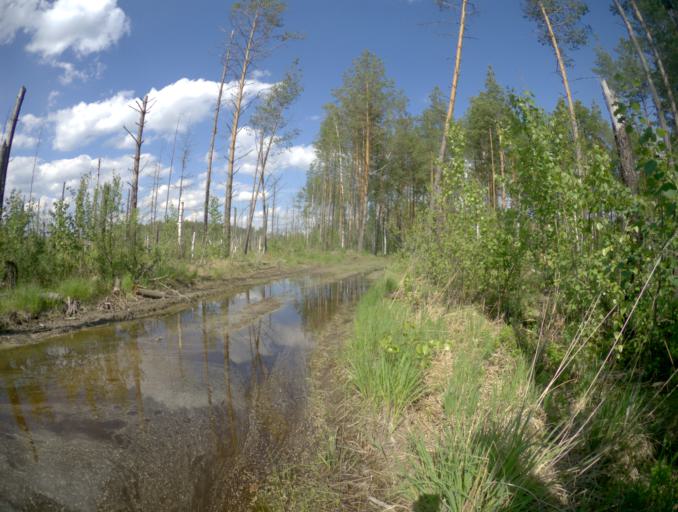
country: RU
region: Vladimir
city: Velikodvorskiy
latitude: 55.3180
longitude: 40.9234
